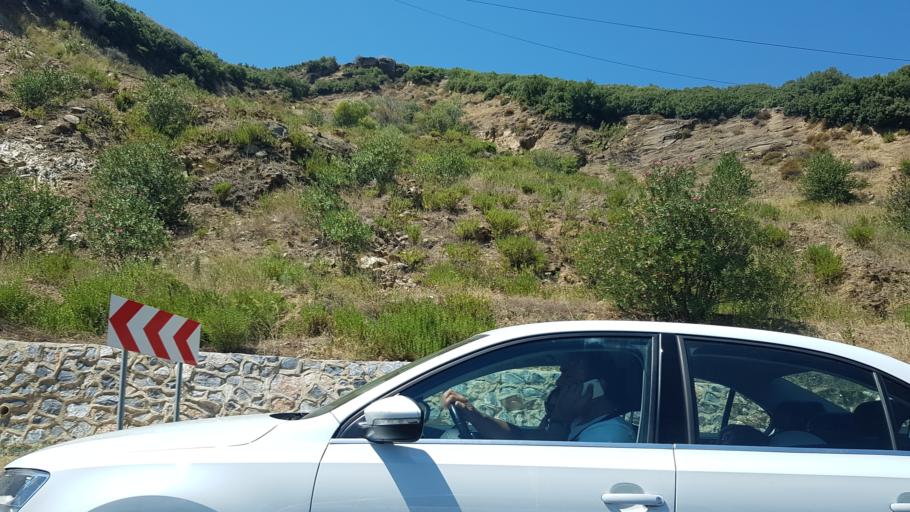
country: TR
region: Aydin
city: Akcaova
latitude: 37.5040
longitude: 28.1029
